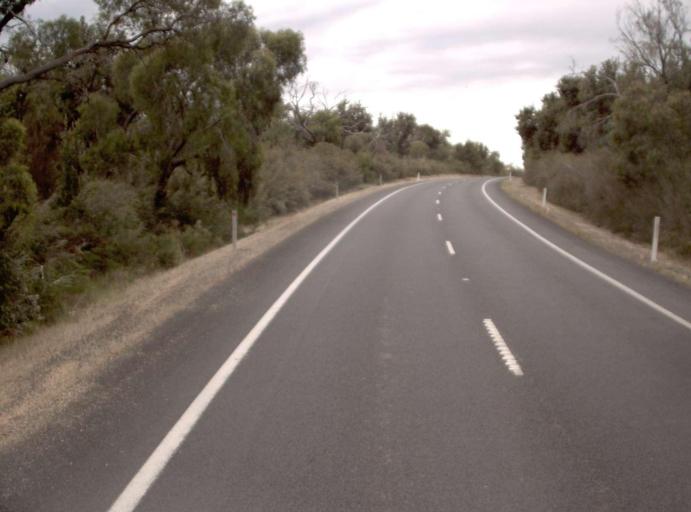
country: AU
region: Victoria
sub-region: Wellington
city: Sale
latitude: -38.2579
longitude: 147.0387
